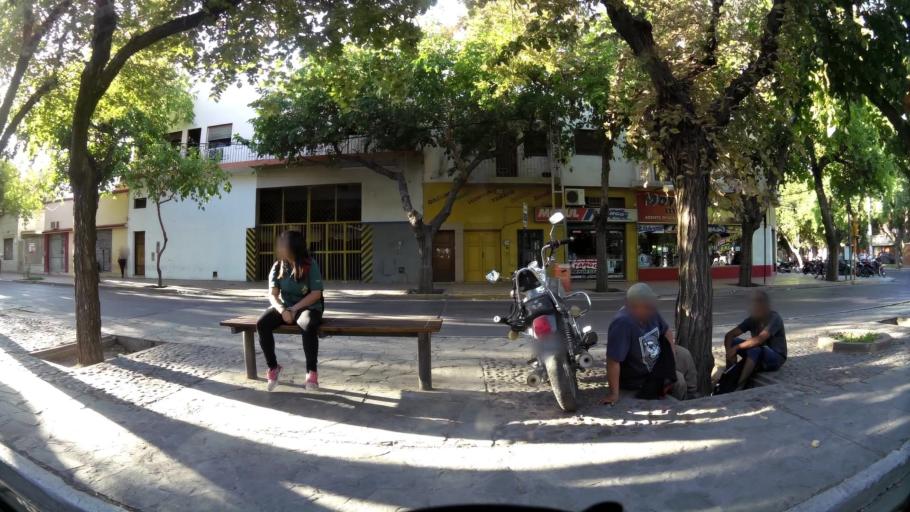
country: AR
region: San Juan
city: San Juan
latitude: -31.5335
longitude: -68.5156
